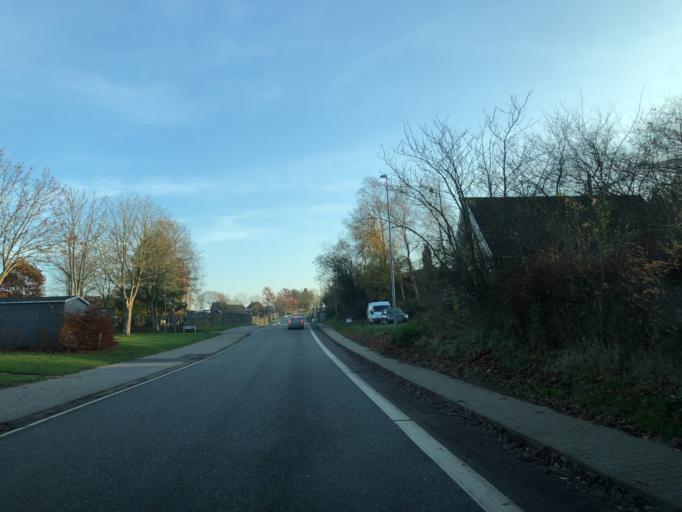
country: DK
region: South Denmark
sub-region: Vejle Kommune
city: Borkop
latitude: 55.5983
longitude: 9.6655
